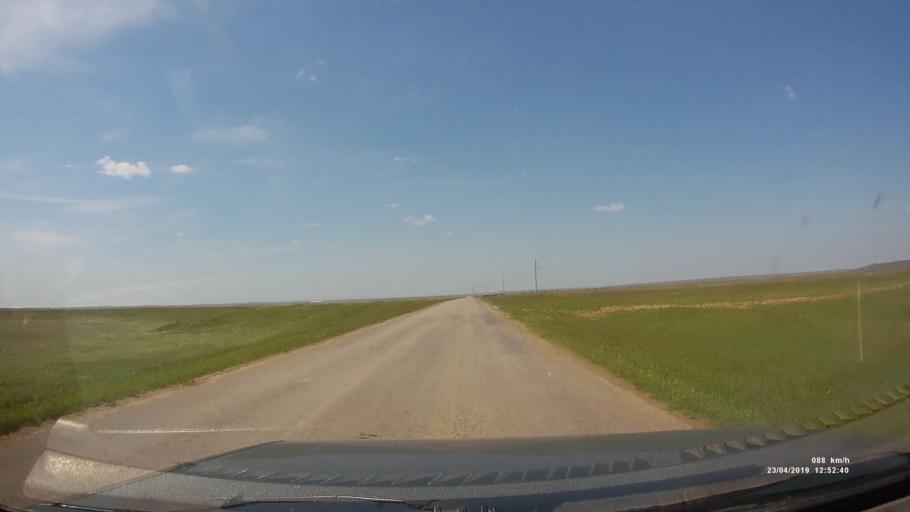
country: RU
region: Kalmykiya
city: Yashalta
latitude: 46.5669
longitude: 42.6064
